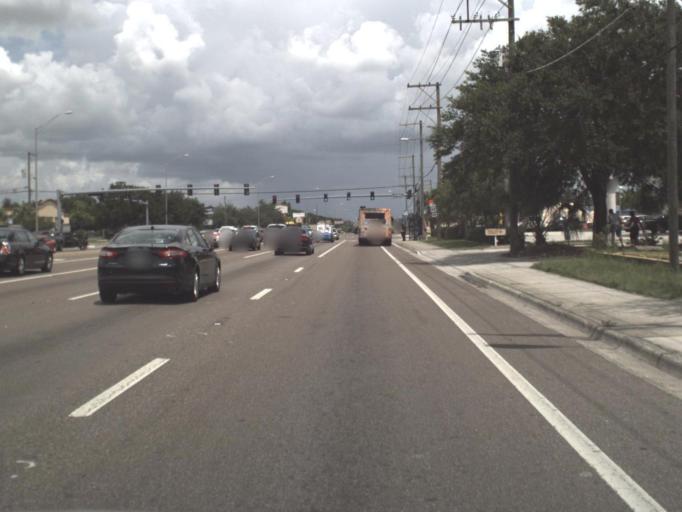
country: US
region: Florida
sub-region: Hillsborough County
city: Egypt Lake-Leto
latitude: 27.9961
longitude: -82.4858
